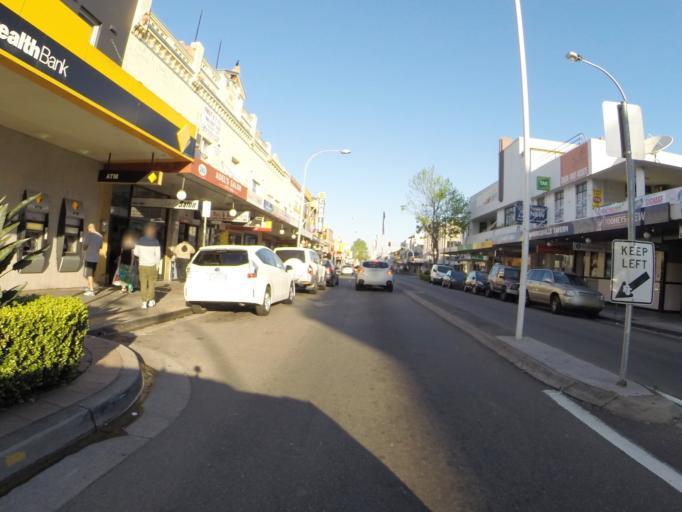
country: AU
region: New South Wales
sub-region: Marrickville
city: Marrickville
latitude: -33.9102
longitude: 151.1556
